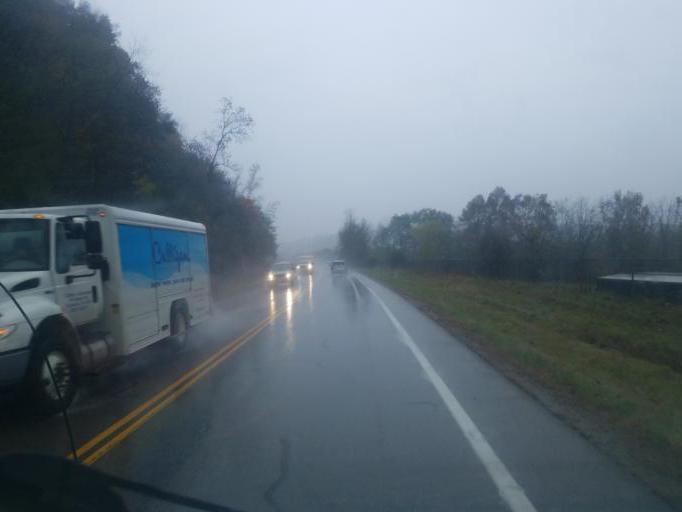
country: US
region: Ohio
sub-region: Muskingum County
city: North Zanesville
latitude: 39.9731
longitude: -82.0539
